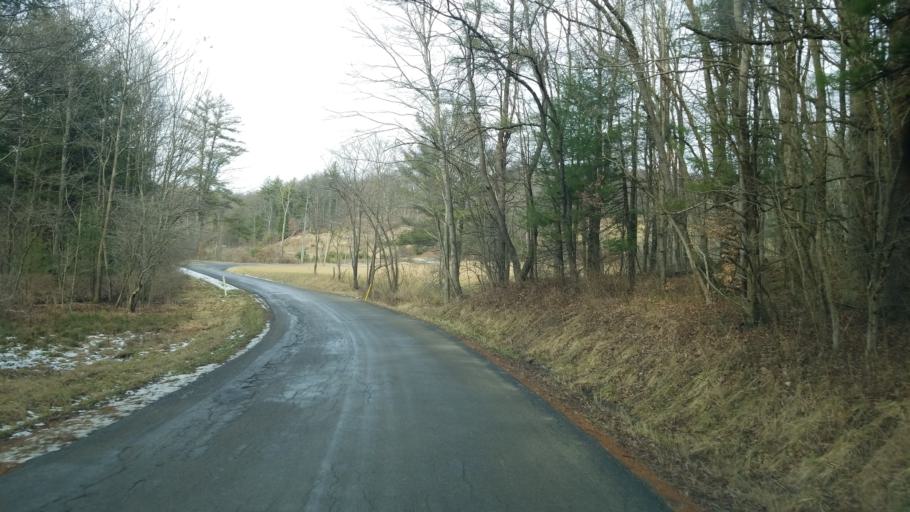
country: US
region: Pennsylvania
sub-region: Jefferson County
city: Punxsutawney
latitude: 40.8464
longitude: -79.0004
